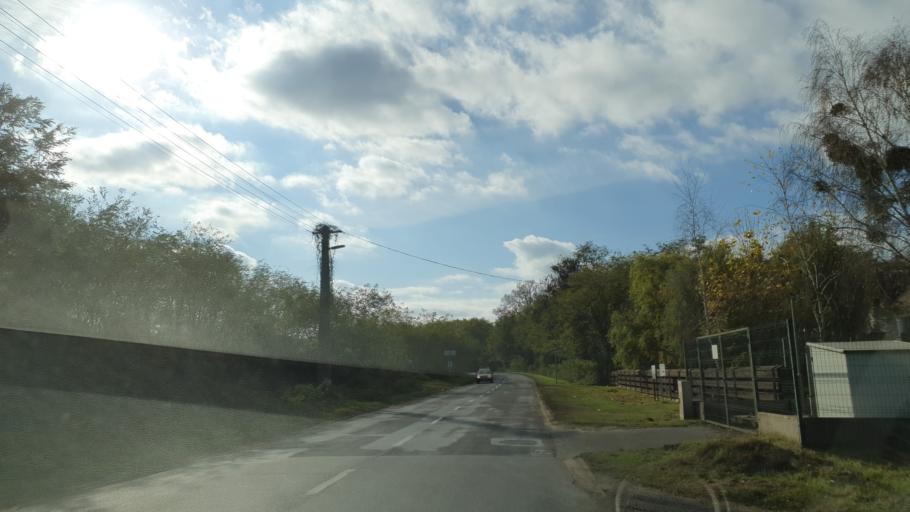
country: HU
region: Szabolcs-Szatmar-Bereg
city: Anarcs
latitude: 48.1680
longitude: 22.0966
